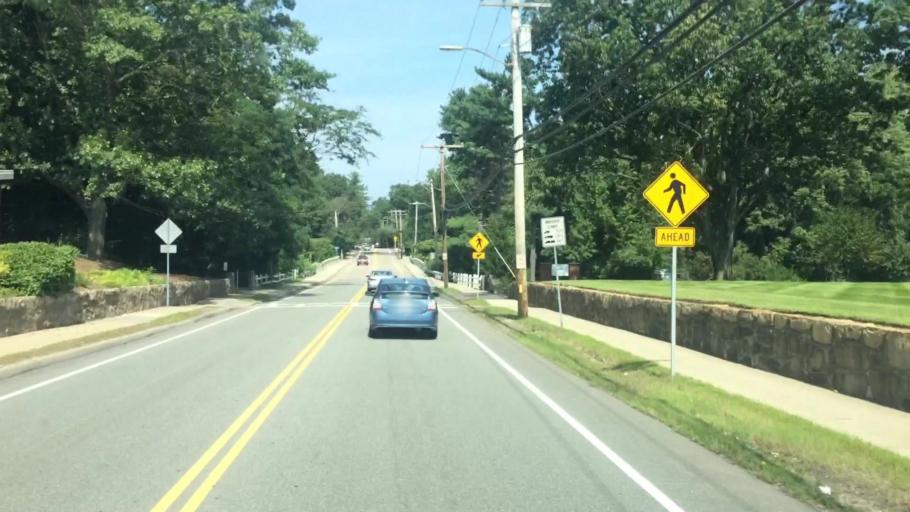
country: US
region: Massachusetts
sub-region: Norfolk County
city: Dedham
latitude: 42.2513
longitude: -71.1758
